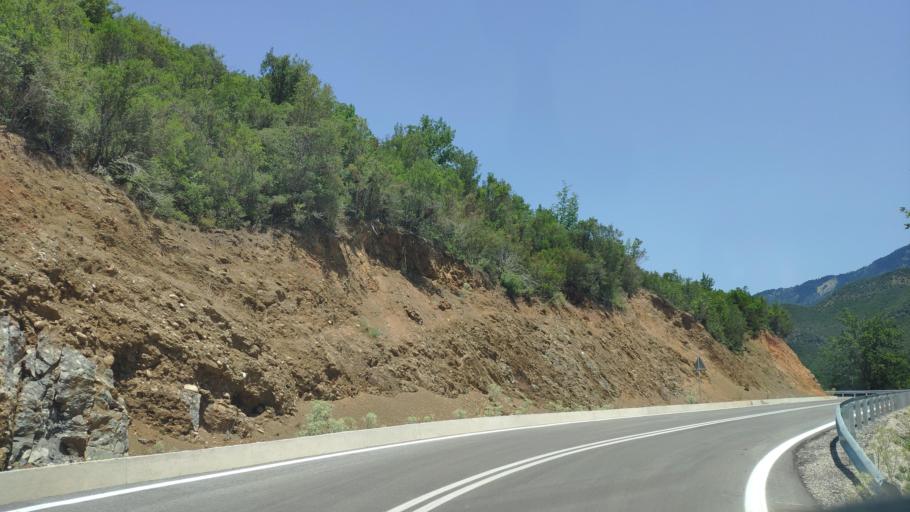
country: GR
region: Epirus
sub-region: Nomos Artas
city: Ano Kalentini
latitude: 39.1842
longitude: 21.3572
